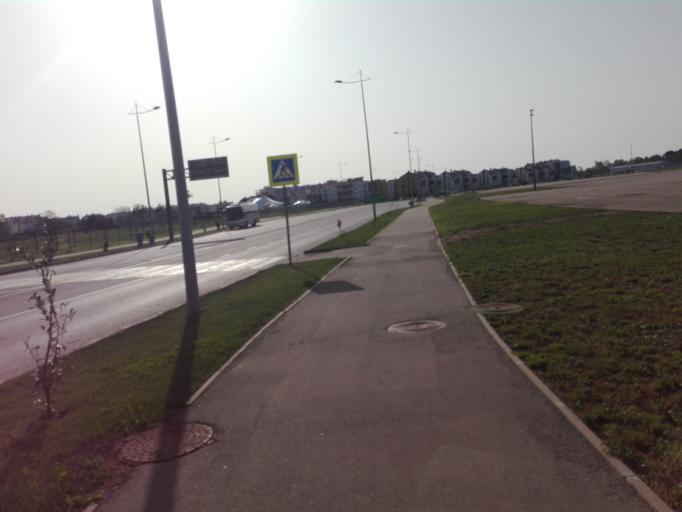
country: RU
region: Krasnodarskiy
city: Adler
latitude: 43.4113
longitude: 39.9484
